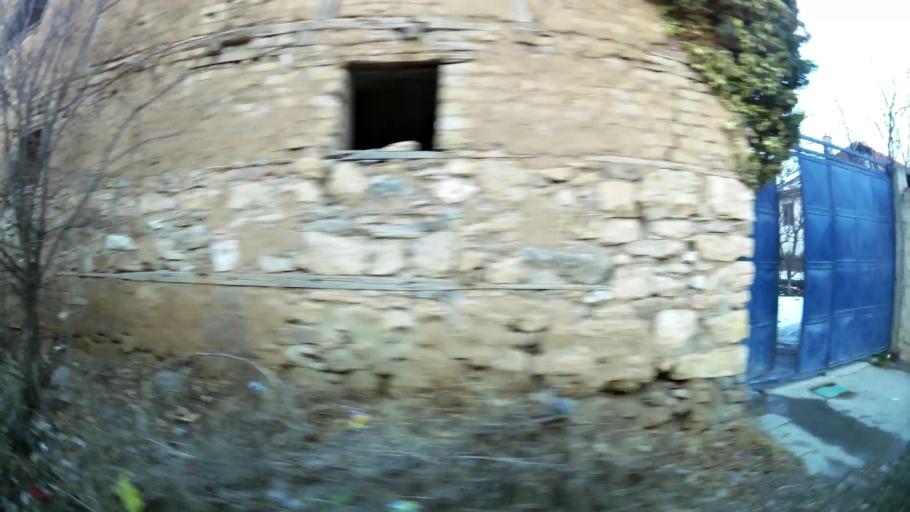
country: MK
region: Aracinovo
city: Arachinovo
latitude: 42.0231
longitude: 21.5659
